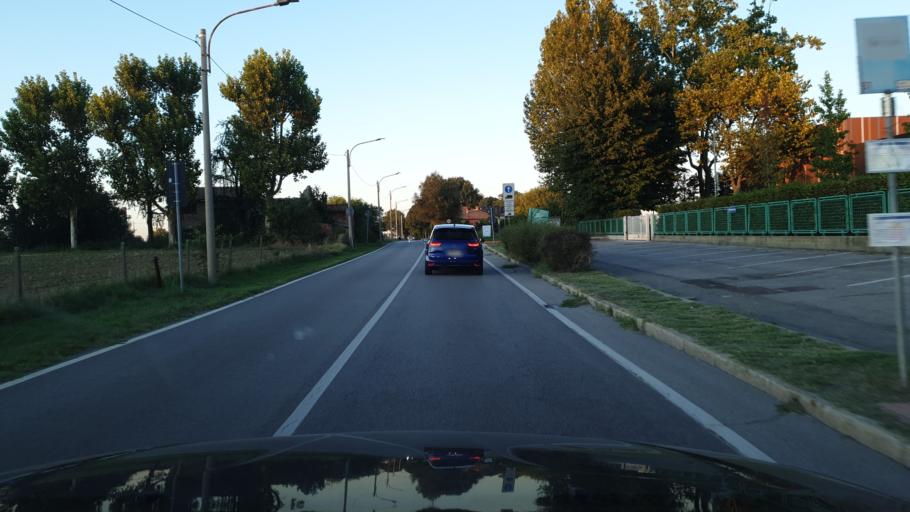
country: IT
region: Emilia-Romagna
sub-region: Provincia di Bologna
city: Quarto Inferiore
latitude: 44.5330
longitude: 11.3884
